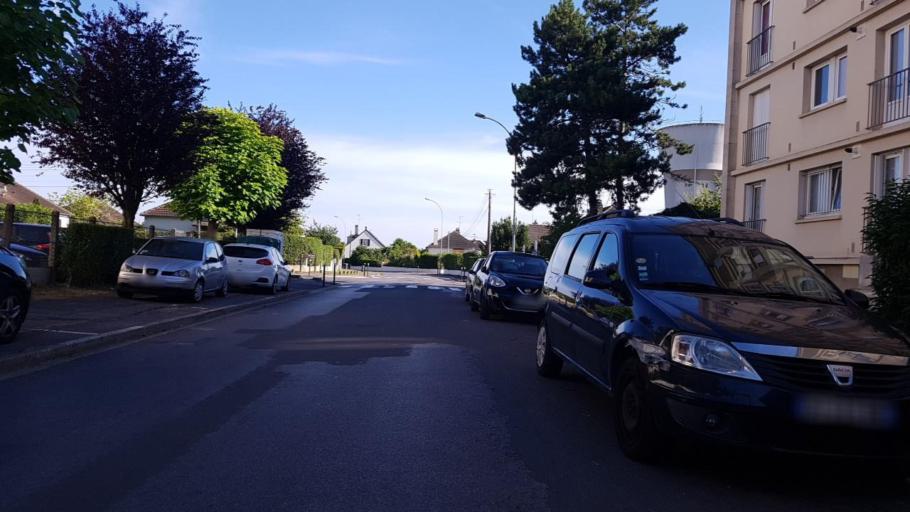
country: FR
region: Picardie
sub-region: Departement de l'Oise
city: Chamant
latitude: 49.2090
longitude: 2.5991
